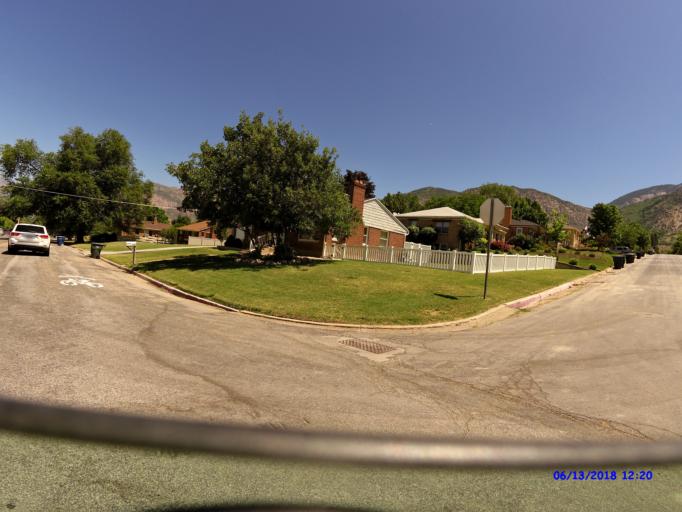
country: US
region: Utah
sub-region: Weber County
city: Ogden
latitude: 41.2110
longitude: -111.9457
